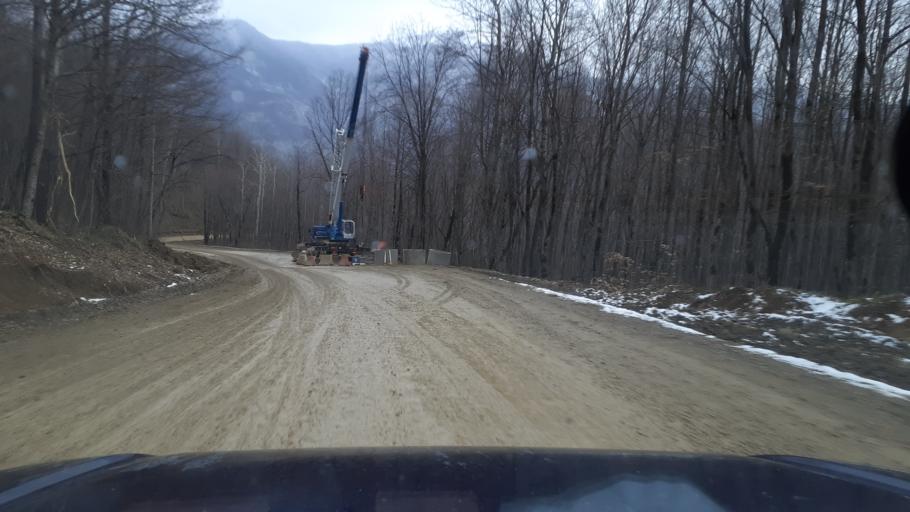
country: RU
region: Krasnodarskiy
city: Neftegorsk
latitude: 44.1653
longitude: 39.8080
